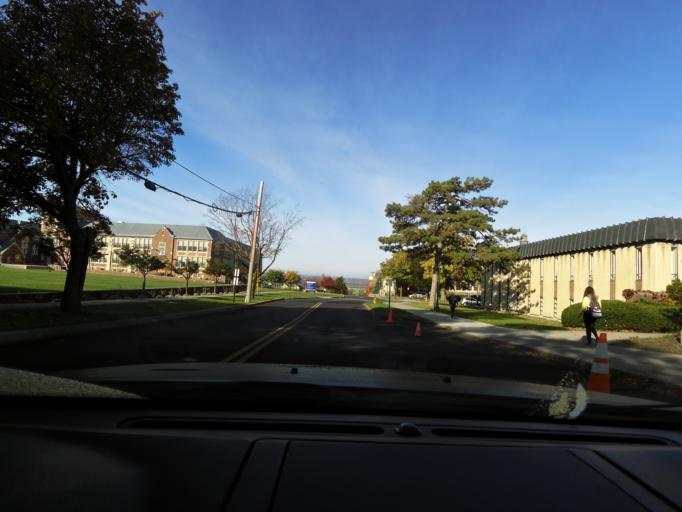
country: US
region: New York
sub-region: Livingston County
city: Geneseo
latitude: 42.7947
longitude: -77.8186
